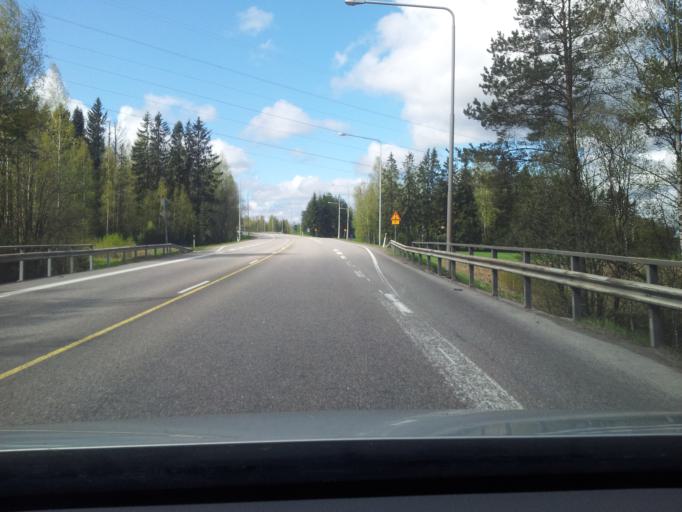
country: FI
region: Kymenlaakso
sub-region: Kouvola
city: Kouvola
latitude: 60.8734
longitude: 26.6088
